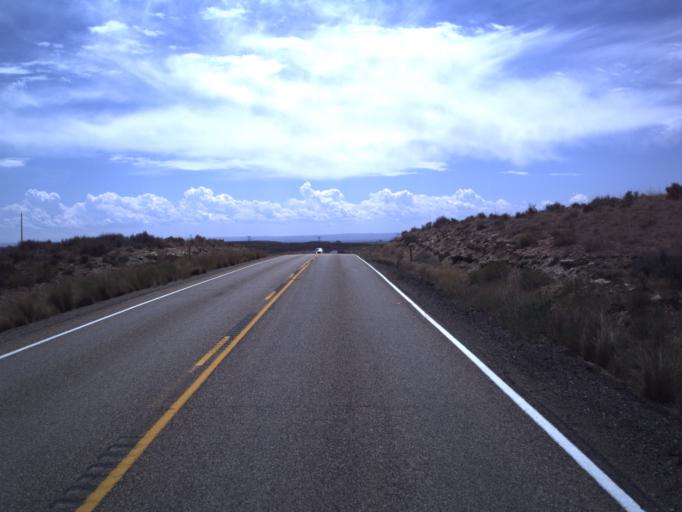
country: US
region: Utah
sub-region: Uintah County
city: Maeser
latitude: 40.2915
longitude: -109.6855
